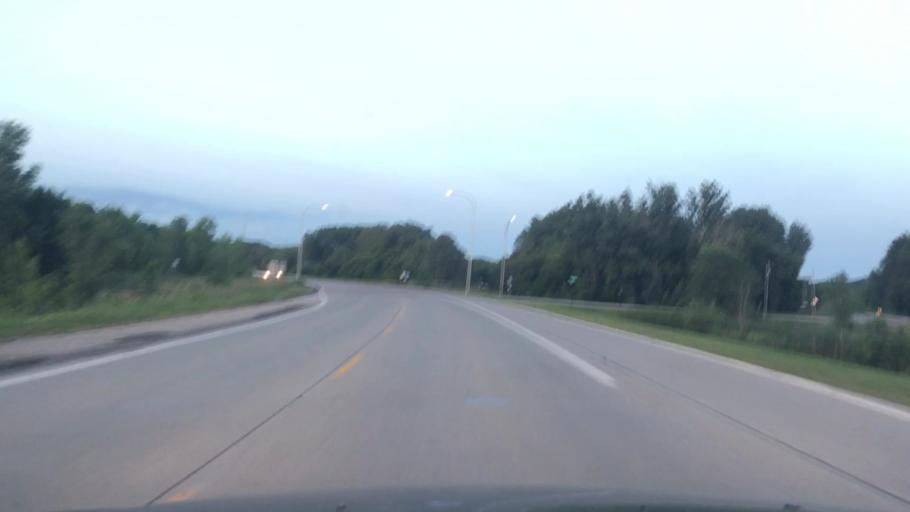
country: US
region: Minnesota
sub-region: Redwood County
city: Redwood Falls
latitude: 44.5401
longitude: -95.0077
